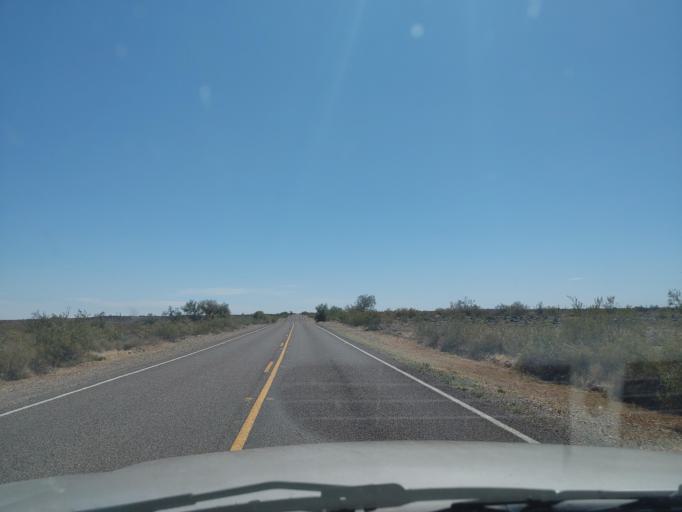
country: US
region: Arizona
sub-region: Maricopa County
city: Gila Bend
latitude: 32.9134
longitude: -113.2754
